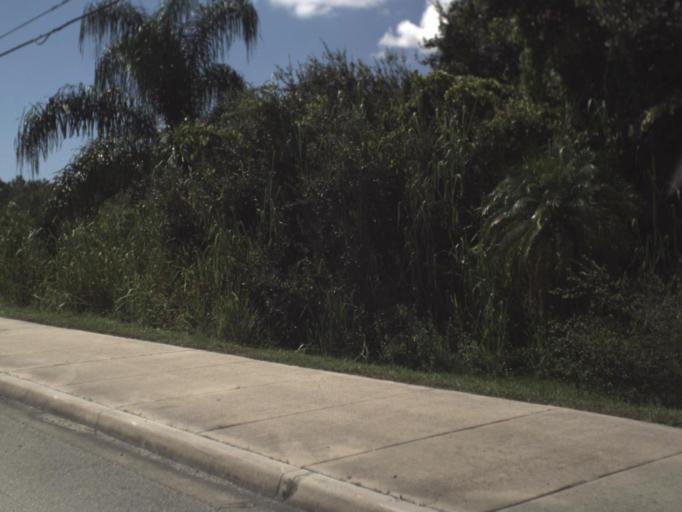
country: US
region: Florida
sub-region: Lee County
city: Suncoast Estates
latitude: 26.7056
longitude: -81.8430
